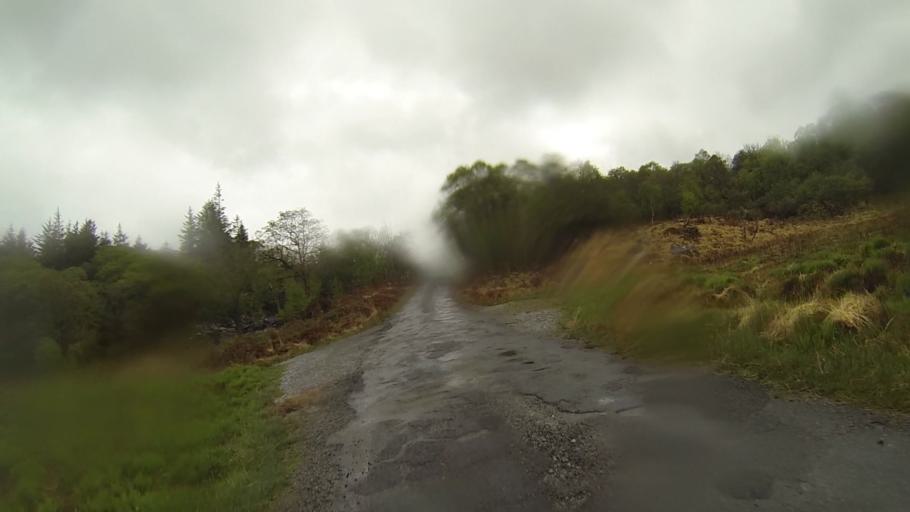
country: IE
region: Munster
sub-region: Ciarrai
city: Kenmare
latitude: 51.9665
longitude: -9.6358
